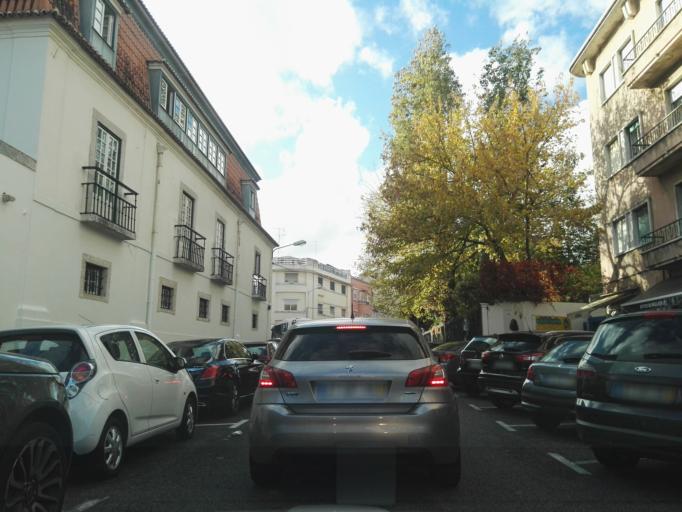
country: PT
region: Lisbon
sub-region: Odivelas
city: Olival do Basto
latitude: 38.7529
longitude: -9.1533
